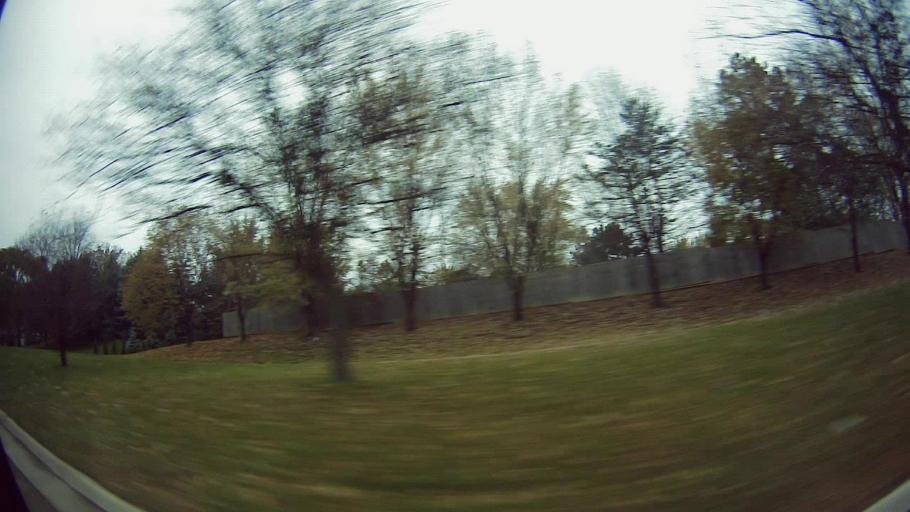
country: US
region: Michigan
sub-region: Oakland County
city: Birmingham
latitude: 42.5611
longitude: -83.1957
